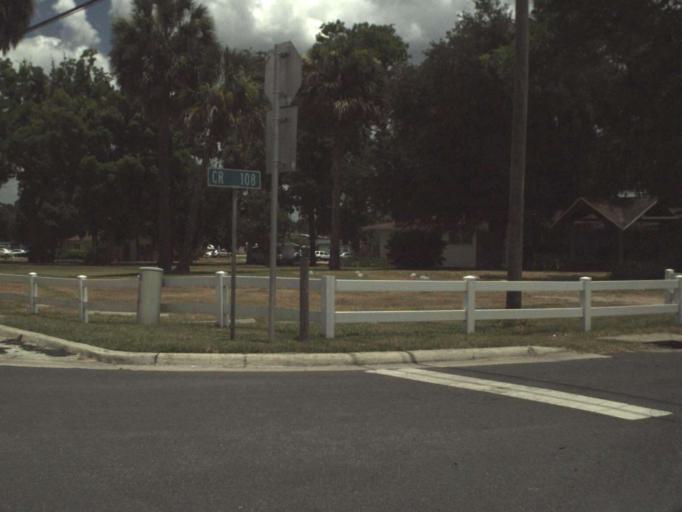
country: US
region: Florida
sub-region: Sumter County
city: Wildwood
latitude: 28.9252
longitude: -82.0372
